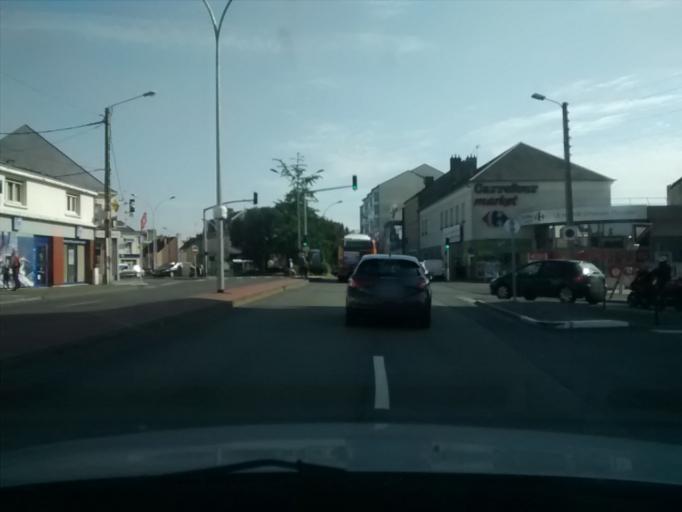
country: FR
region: Pays de la Loire
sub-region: Departement de la Sarthe
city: Le Mans
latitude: 48.0146
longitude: 0.1867
